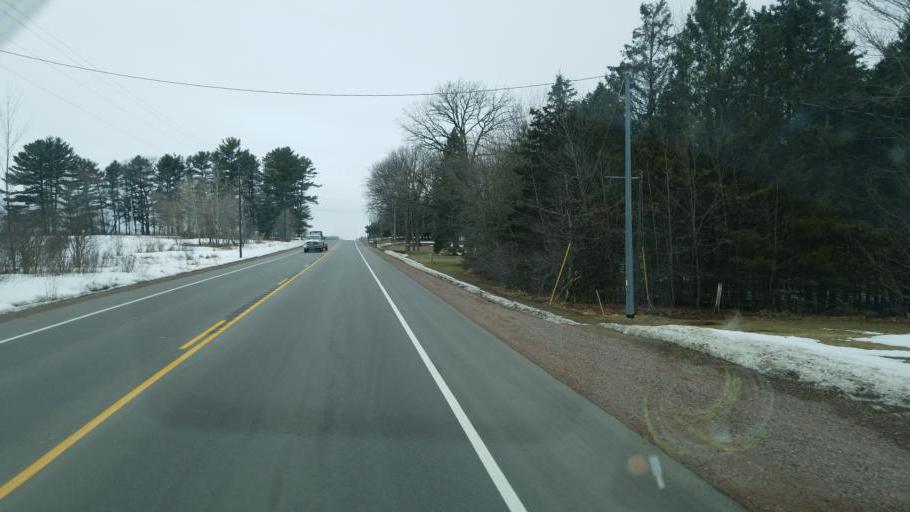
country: US
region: Wisconsin
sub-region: Wood County
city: Marshfield
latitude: 44.6564
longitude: -90.2596
